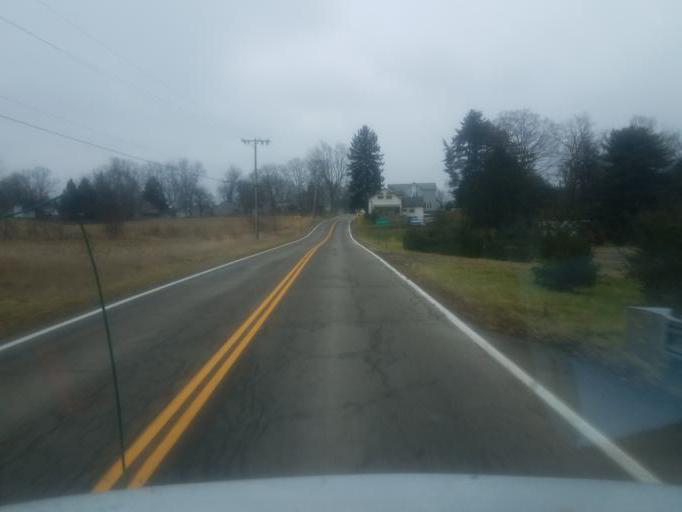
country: US
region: Ohio
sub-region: Ashland County
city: Ashland
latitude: 40.8870
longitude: -82.4307
